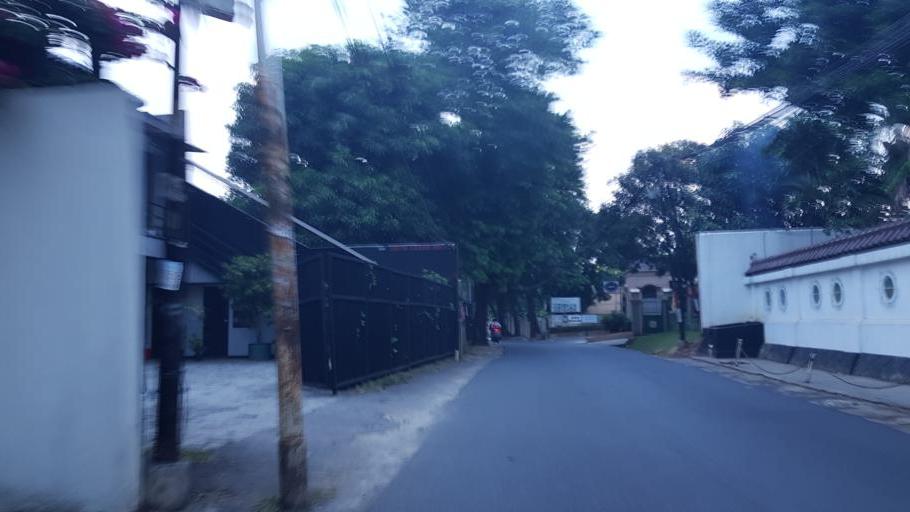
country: ID
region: West Java
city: Pamulang
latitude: -6.2979
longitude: 106.7926
